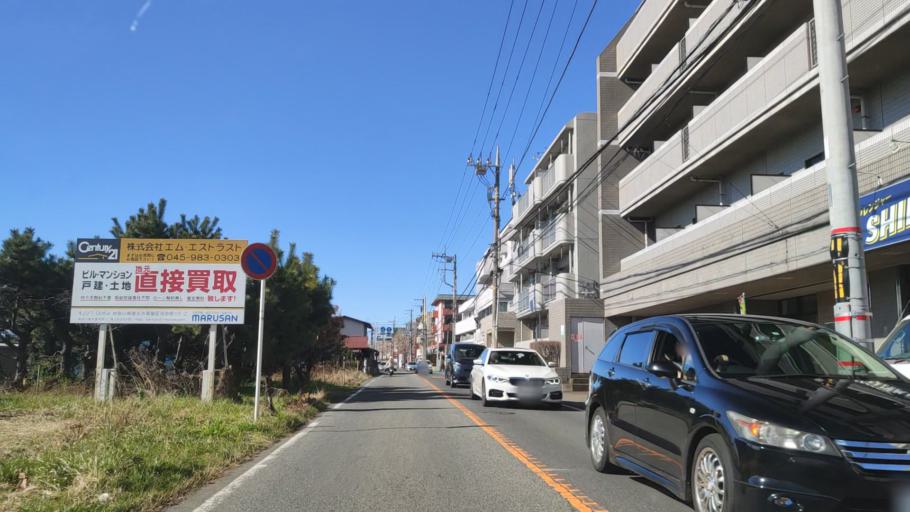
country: JP
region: Tokyo
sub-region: Machida-shi
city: Machida
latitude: 35.5373
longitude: 139.5034
